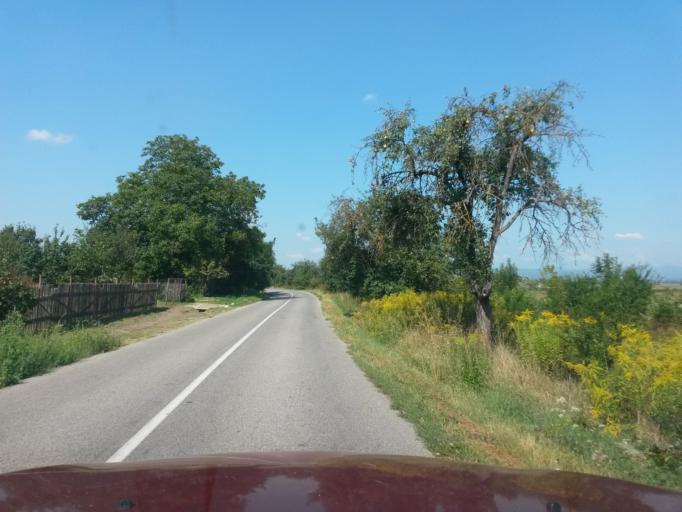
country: SK
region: Kosicky
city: Moldava nad Bodvou
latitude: 48.5310
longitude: 21.1246
